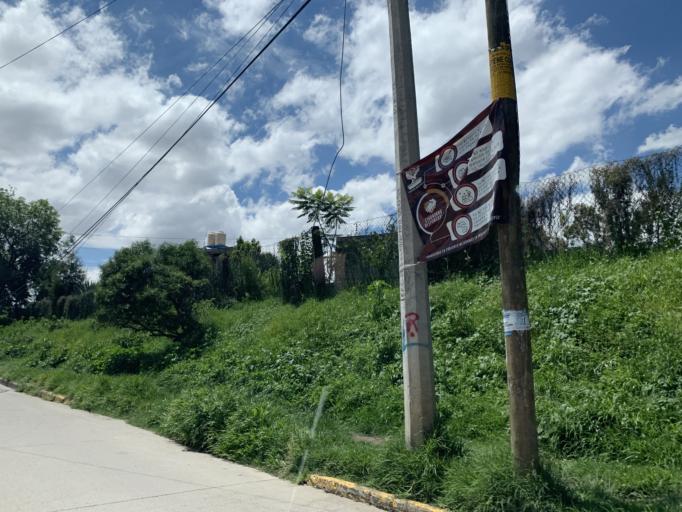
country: MX
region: Puebla
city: Cuautlancingo
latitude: 19.0833
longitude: -98.2702
